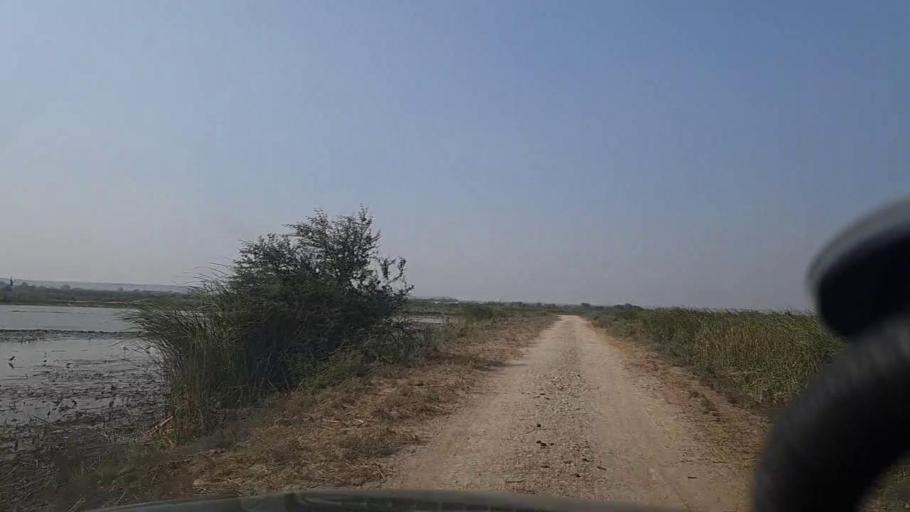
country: PK
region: Sindh
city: Thatta
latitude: 24.6160
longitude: 67.8853
